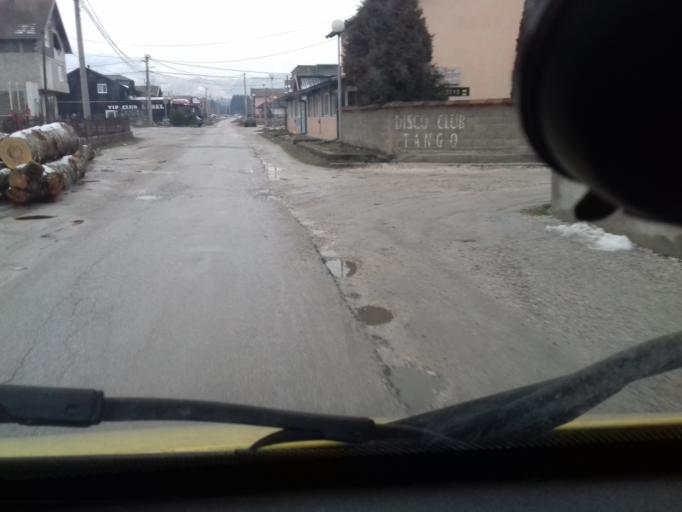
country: BA
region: Federation of Bosnia and Herzegovina
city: Vitez
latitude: 44.1562
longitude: 17.7836
